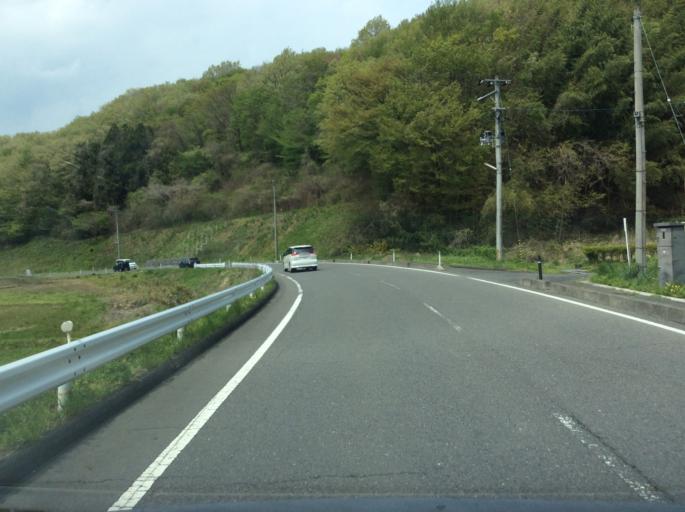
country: JP
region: Fukushima
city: Miharu
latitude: 37.3990
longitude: 140.4762
